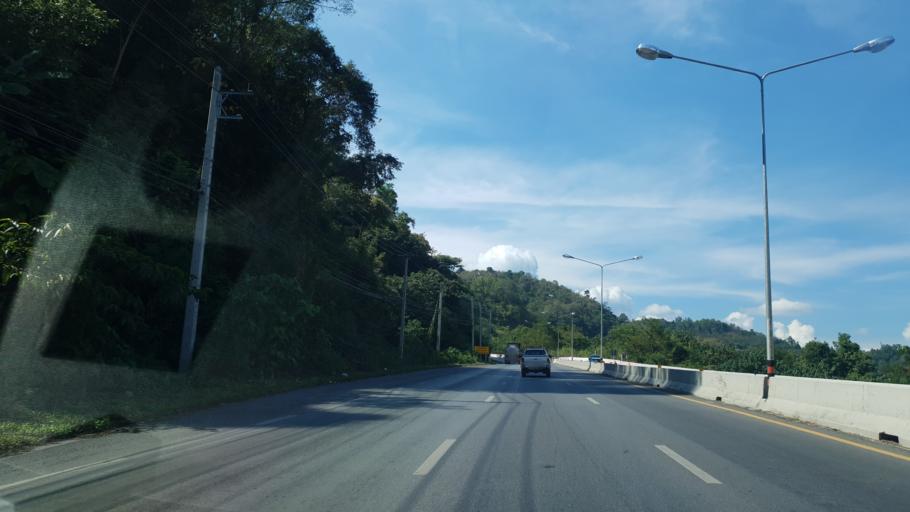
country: TH
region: Phrae
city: Den Chai
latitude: 17.8254
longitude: 100.0709
